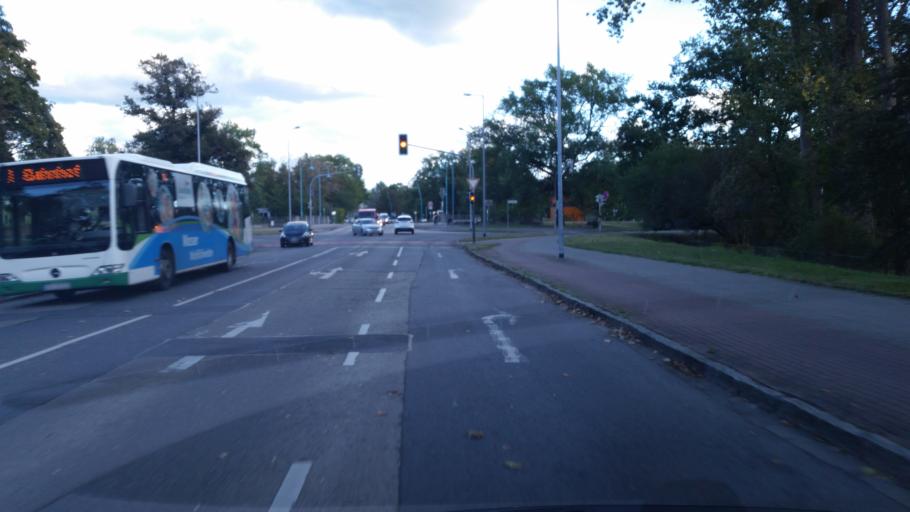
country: DE
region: Saxony
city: Hoyerswerda
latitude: 51.4394
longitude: 14.2520
